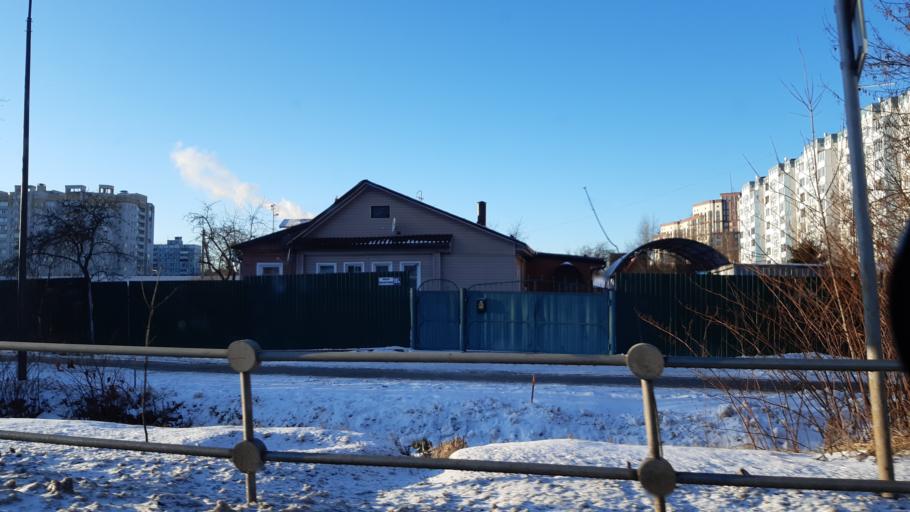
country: RU
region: Moskovskaya
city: Sergiyev Posad
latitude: 56.3266
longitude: 38.1494
